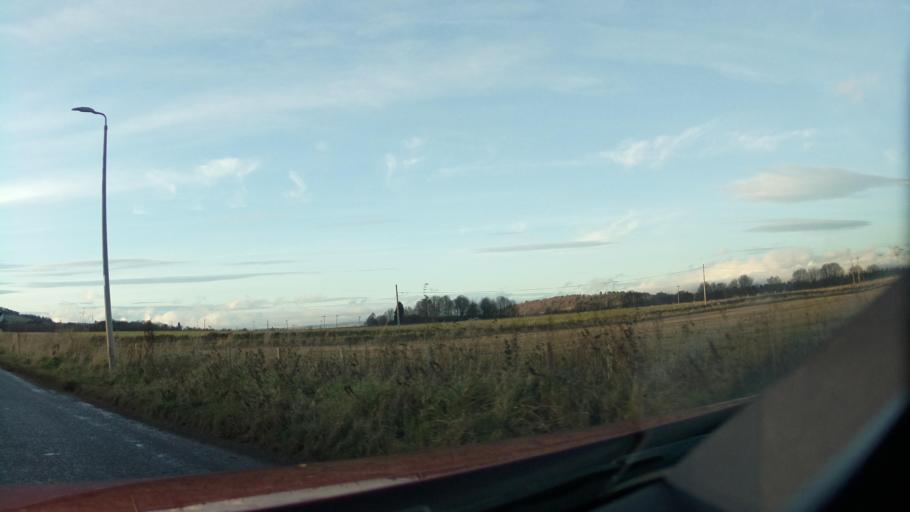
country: GB
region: Scotland
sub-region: Angus
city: Forfar
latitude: 56.5865
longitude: -2.8989
